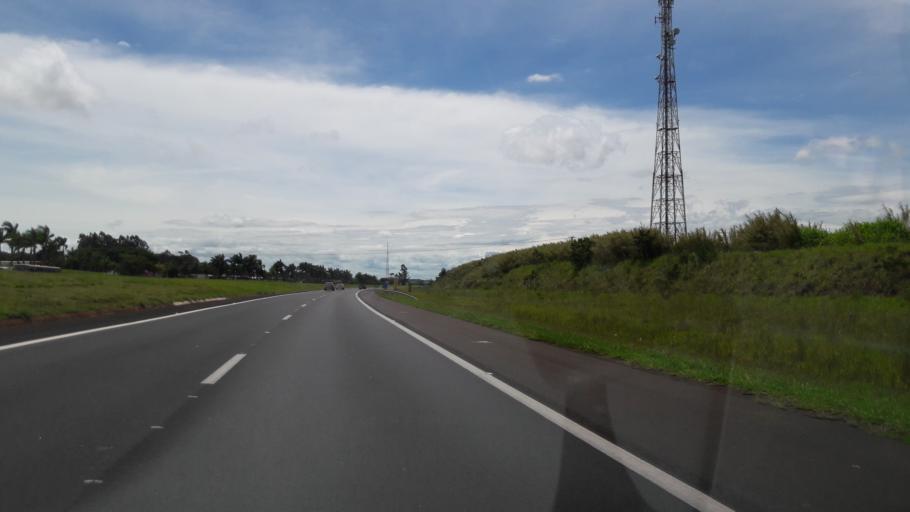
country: BR
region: Sao Paulo
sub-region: Avare
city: Avare
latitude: -22.9572
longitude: -48.8595
